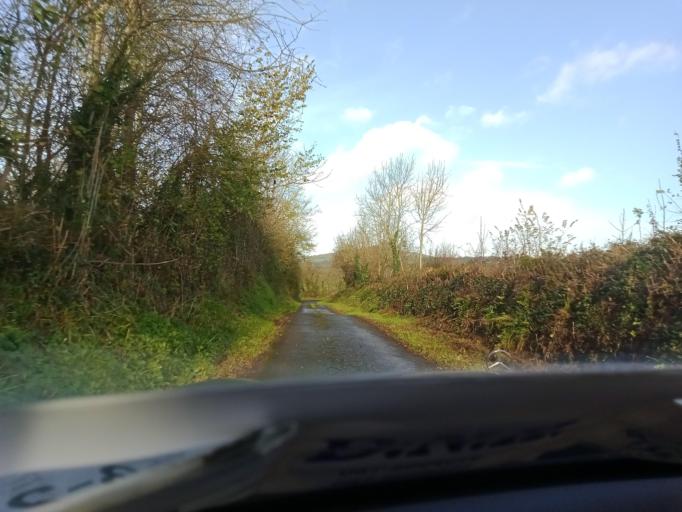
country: IE
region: Leinster
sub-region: Kilkenny
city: Mooncoin
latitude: 52.3312
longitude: -7.2801
